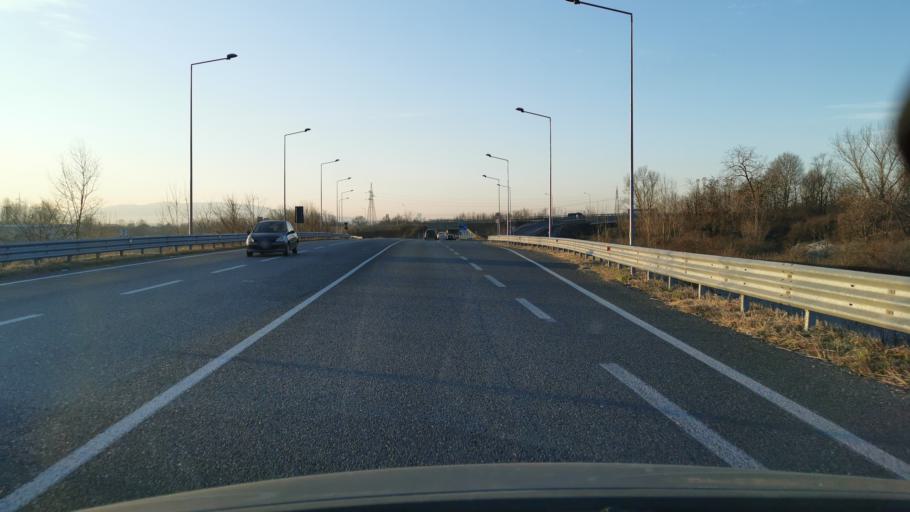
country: IT
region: Piedmont
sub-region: Provincia di Torino
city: Borgaro Torinese
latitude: 45.1508
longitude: 7.6447
